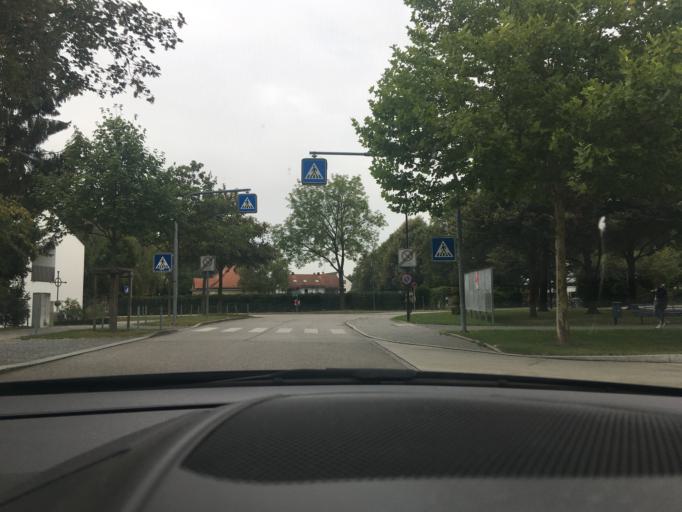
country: DE
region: Bavaria
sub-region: Upper Bavaria
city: Ismaning
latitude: 48.2263
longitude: 11.6791
